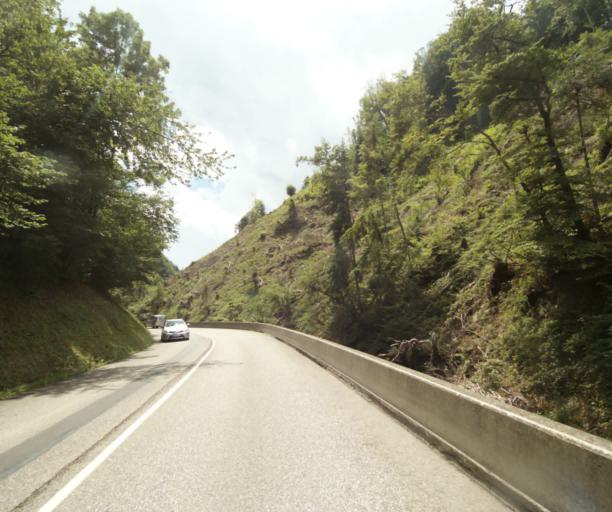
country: FR
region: Rhone-Alpes
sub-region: Departement de la Haute-Savoie
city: Thones
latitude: 45.8595
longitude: 6.3286
